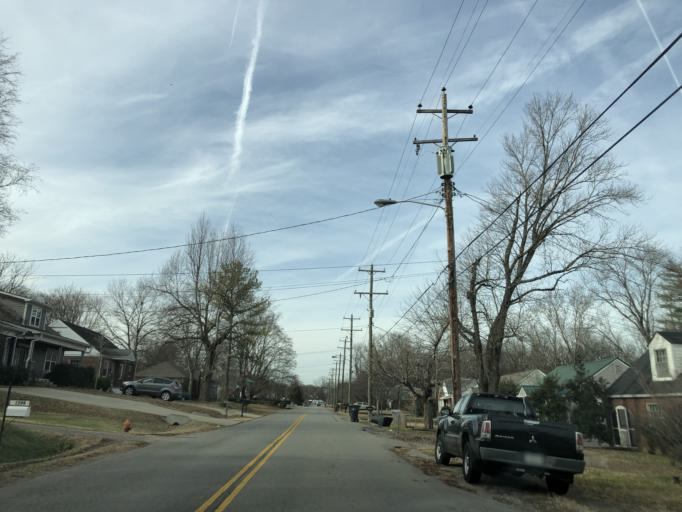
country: US
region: Tennessee
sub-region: Davidson County
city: Nashville
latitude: 36.2173
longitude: -86.7230
